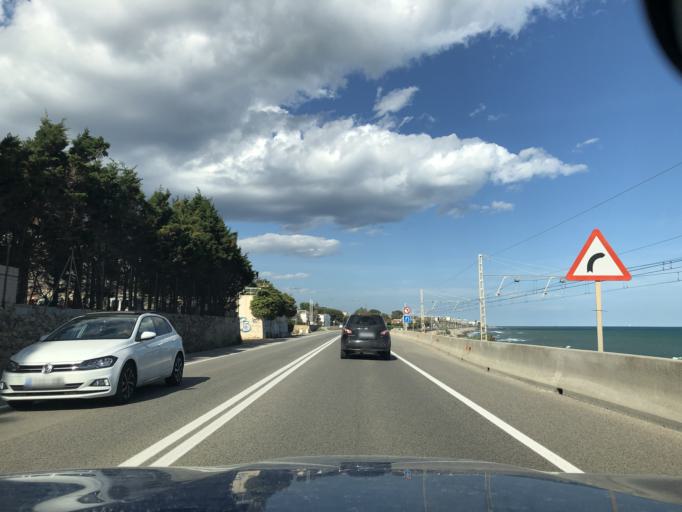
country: ES
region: Catalonia
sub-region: Provincia de Barcelona
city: Mataro
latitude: 41.5457
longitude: 2.4670
